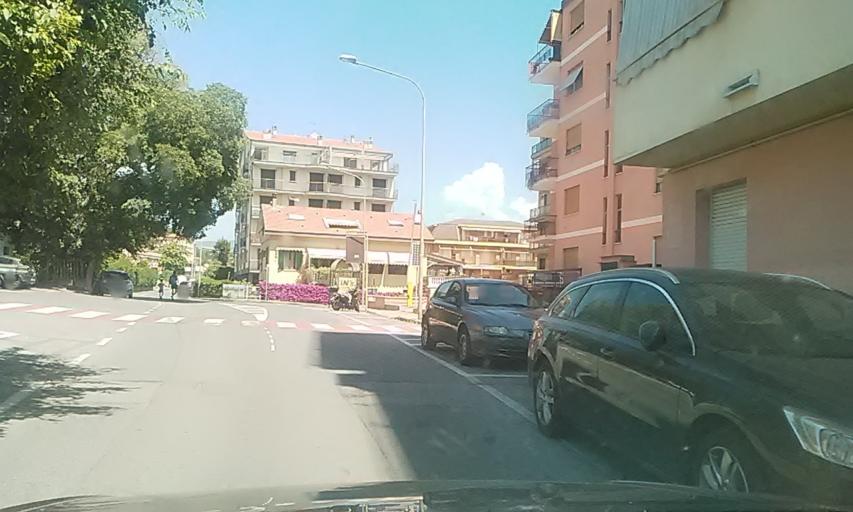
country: IT
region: Liguria
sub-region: Provincia di Savona
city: Andora
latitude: 43.9518
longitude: 8.1398
